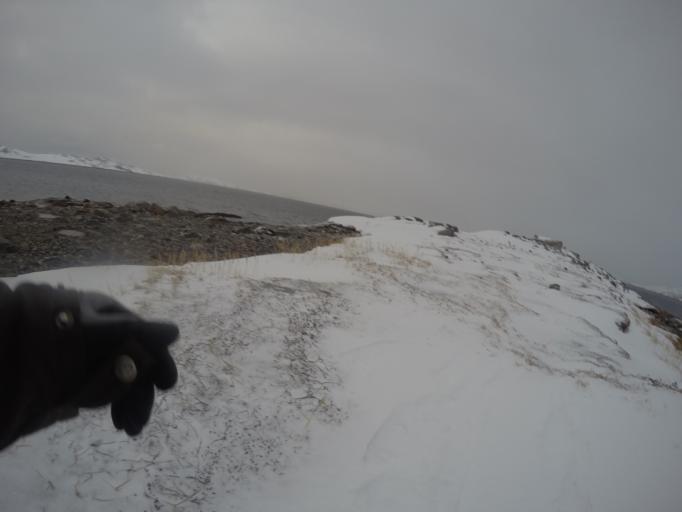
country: GL
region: Sermersooq
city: Nuuk
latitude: 64.1426
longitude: -51.6790
